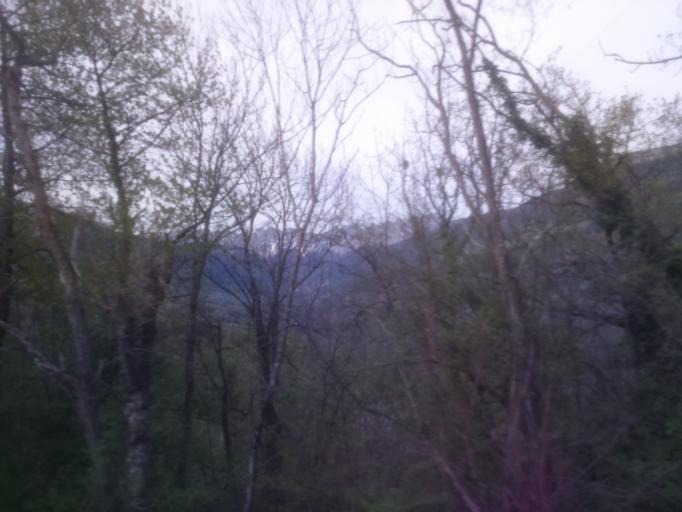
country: FR
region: Rhone-Alpes
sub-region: Departement de l'Isere
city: Le Gua
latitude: 44.9667
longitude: 5.6373
